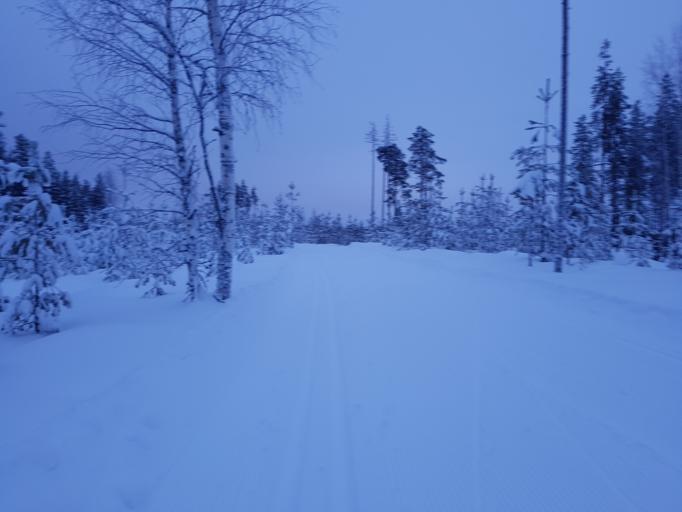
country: FI
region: Kainuu
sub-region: Kehys-Kainuu
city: Kuhmo
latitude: 64.0873
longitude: 29.5160
